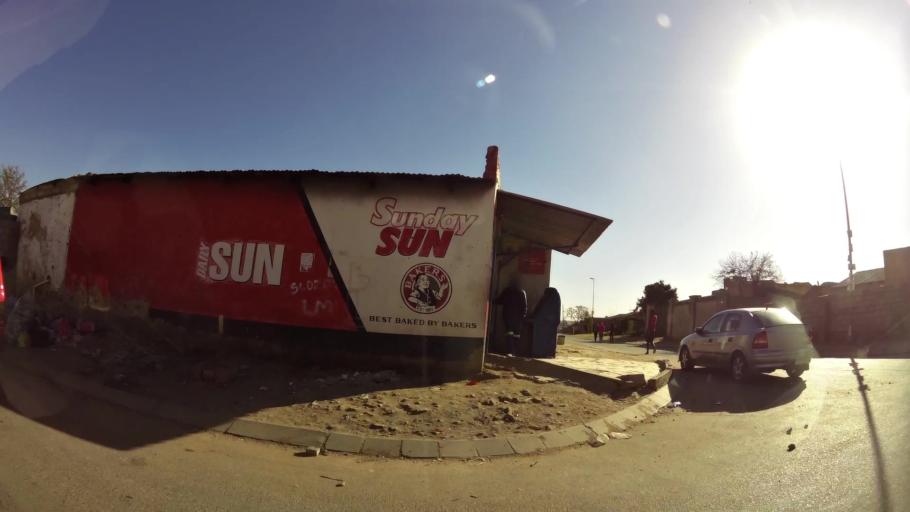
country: ZA
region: Gauteng
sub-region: Ekurhuleni Metropolitan Municipality
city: Tembisa
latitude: -26.0293
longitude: 28.2151
